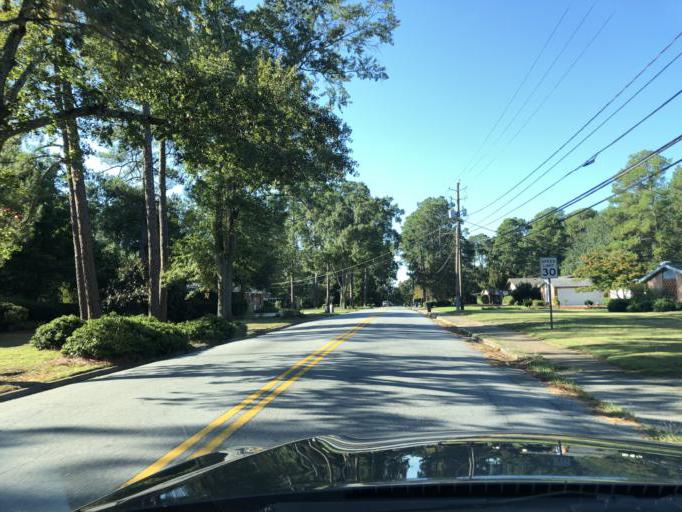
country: US
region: Georgia
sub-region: Muscogee County
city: Columbus
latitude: 32.4881
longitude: -84.9455
